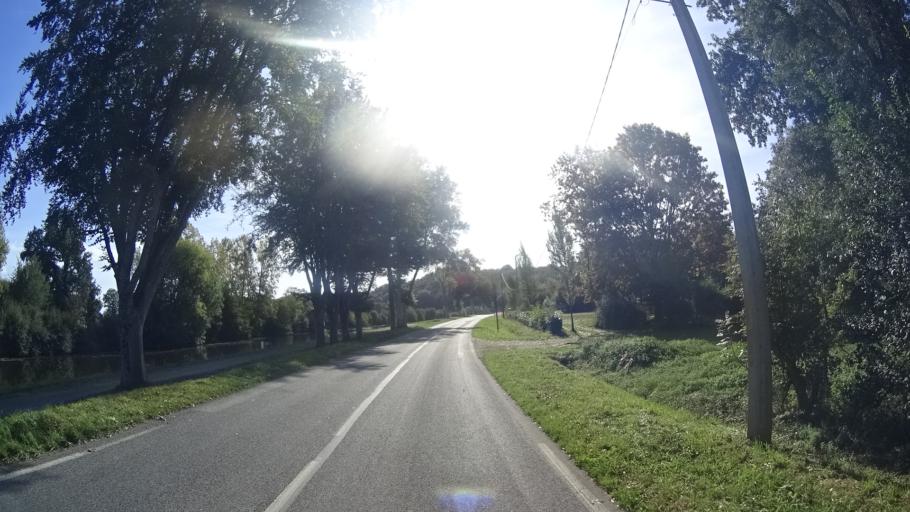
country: FR
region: Brittany
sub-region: Departement du Morbihan
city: Peillac
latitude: 47.7282
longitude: -2.2142
